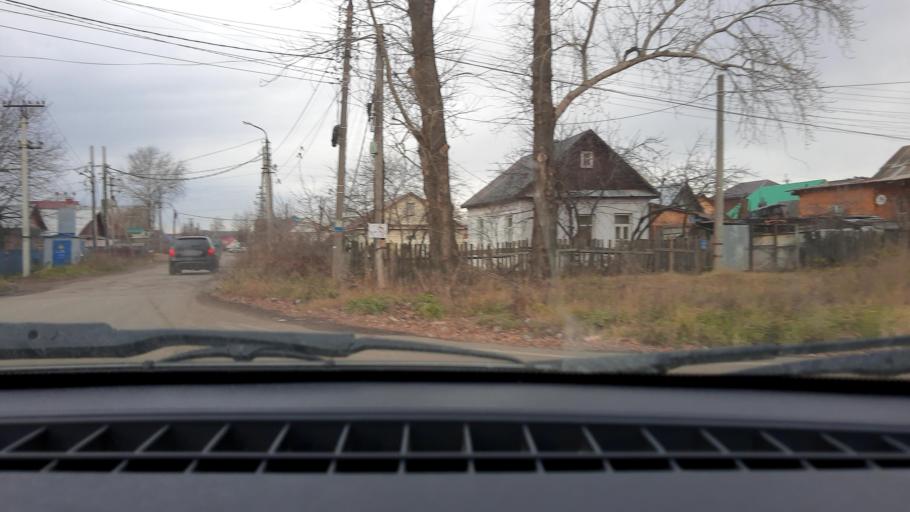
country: RU
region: Bashkortostan
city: Iglino
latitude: 54.8272
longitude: 56.1854
